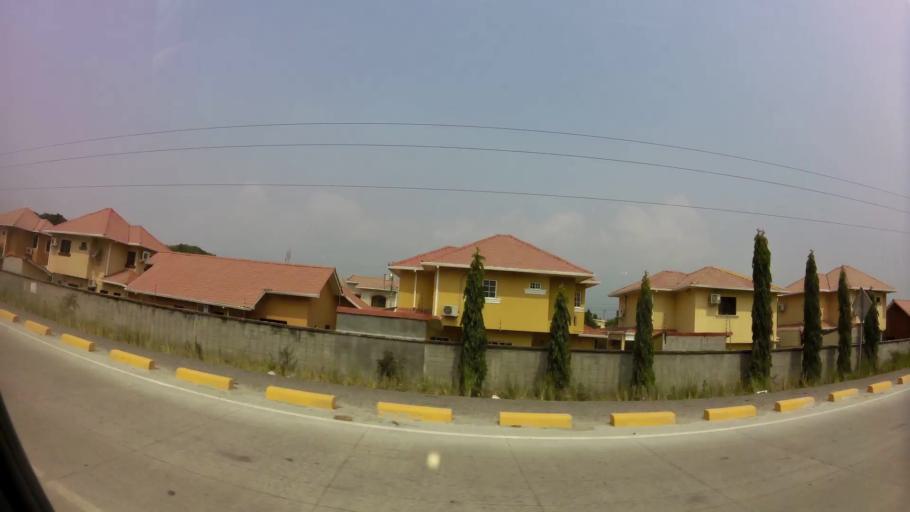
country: HN
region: Cortes
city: San Pedro Sula
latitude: 15.5476
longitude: -87.9980
